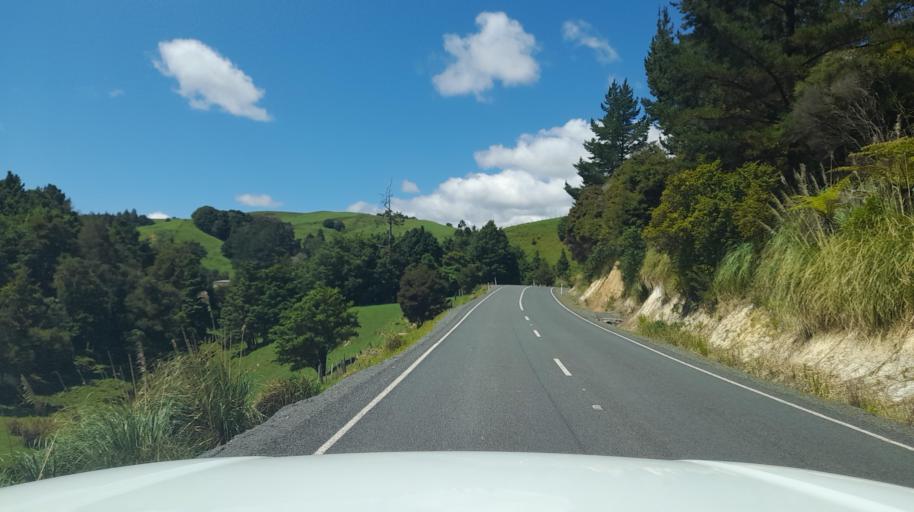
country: NZ
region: Northland
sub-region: Far North District
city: Taipa
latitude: -35.0977
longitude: 173.4696
